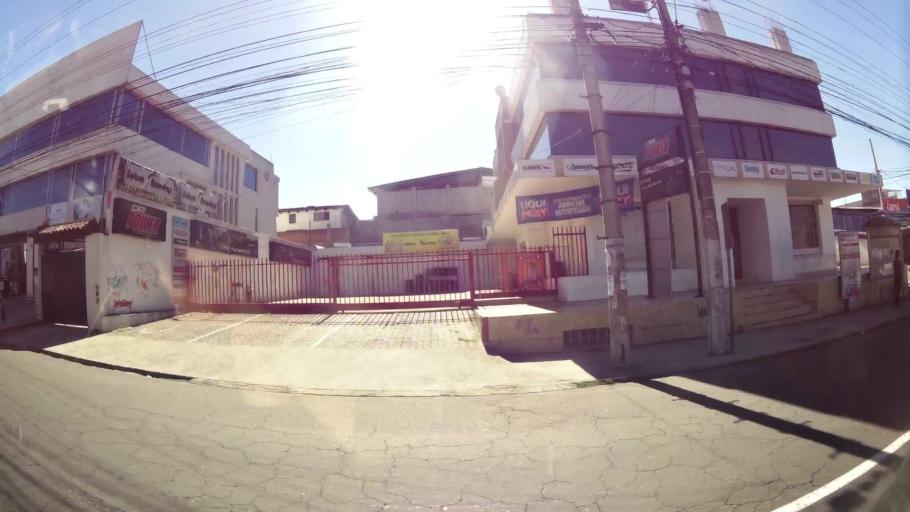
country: EC
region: Pichincha
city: Quito
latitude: -0.1612
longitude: -78.4763
